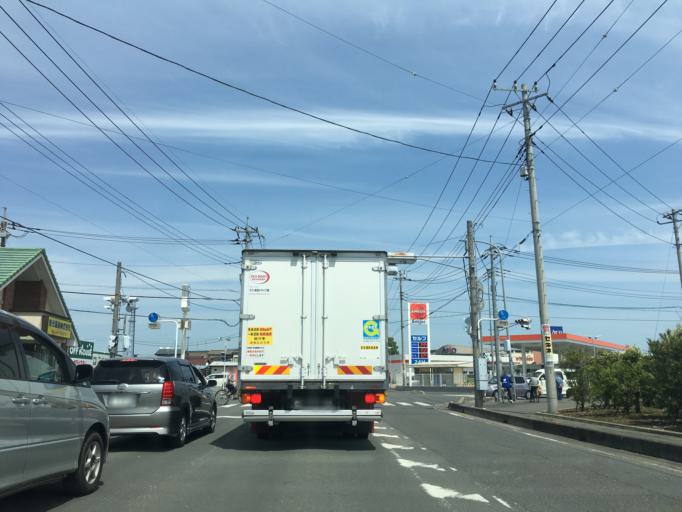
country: JP
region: Saitama
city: Okegawa
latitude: 35.9585
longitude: 139.5644
